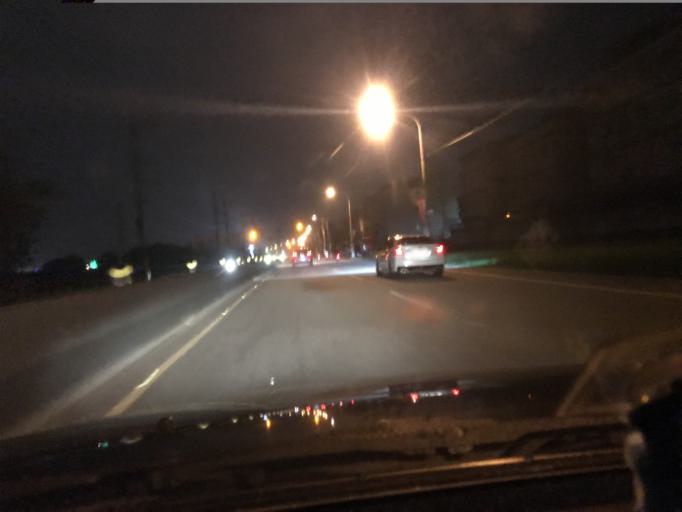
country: TW
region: Taiwan
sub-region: Hsinchu
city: Zhubei
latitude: 24.7805
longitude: 121.0695
